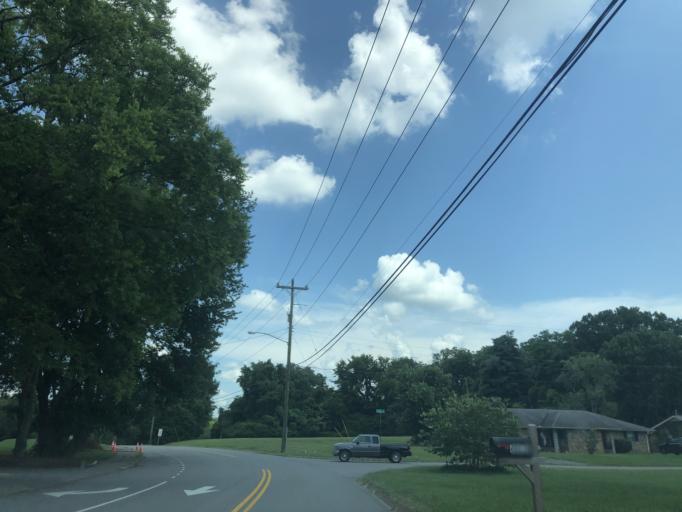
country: US
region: Tennessee
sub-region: Davidson County
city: Lakewood
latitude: 36.1977
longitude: -86.6106
